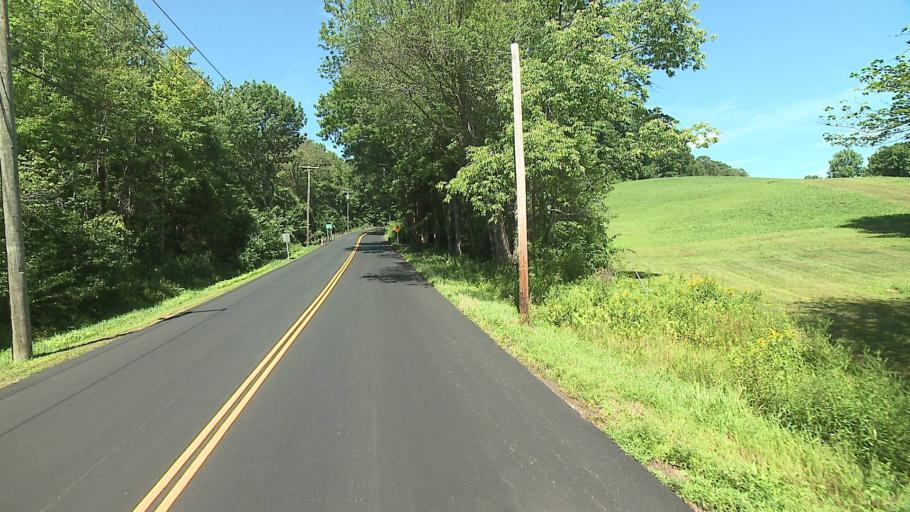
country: US
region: Connecticut
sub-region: Hartford County
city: West Simsbury
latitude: 41.9196
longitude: -72.9064
